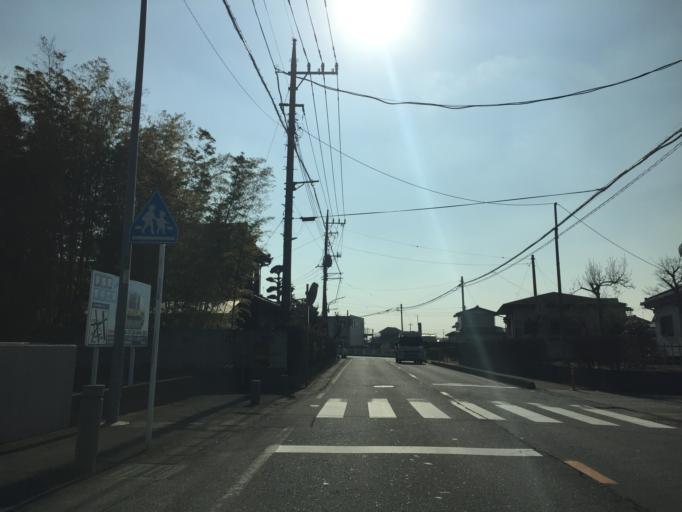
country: JP
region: Saitama
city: Shiki
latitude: 35.8605
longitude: 139.5604
